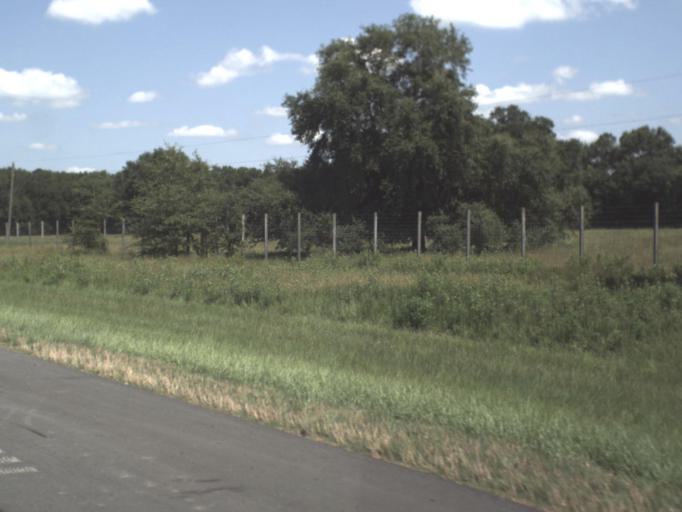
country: US
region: Florida
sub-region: Madison County
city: Madison
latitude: 30.4013
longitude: -83.3821
